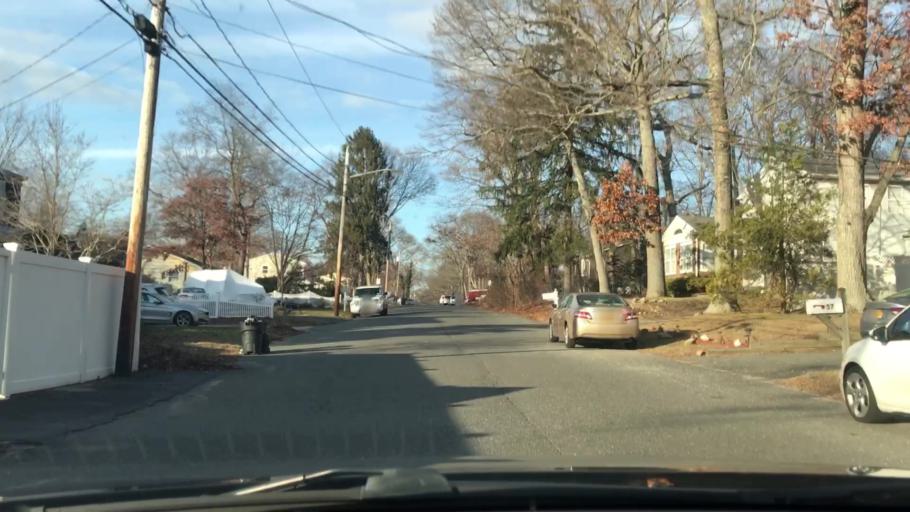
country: US
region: New York
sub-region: Suffolk County
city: Centereach
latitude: 40.8436
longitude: -73.1010
